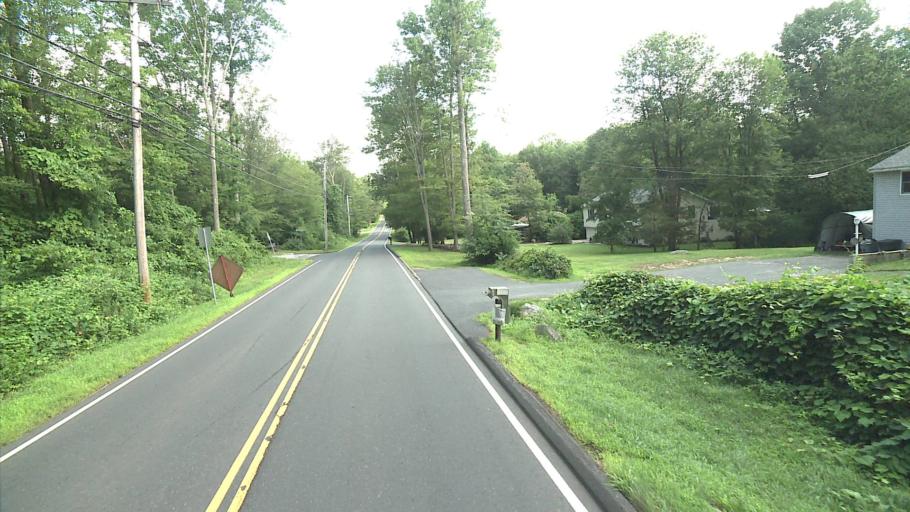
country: US
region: Connecticut
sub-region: Middlesex County
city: Moodus
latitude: 41.5485
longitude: -72.4127
